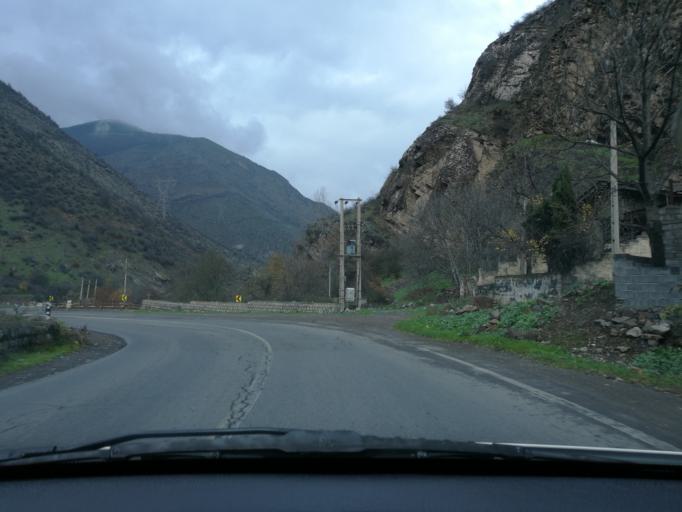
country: IR
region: Mazandaran
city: Chalus
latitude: 36.3401
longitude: 51.2585
